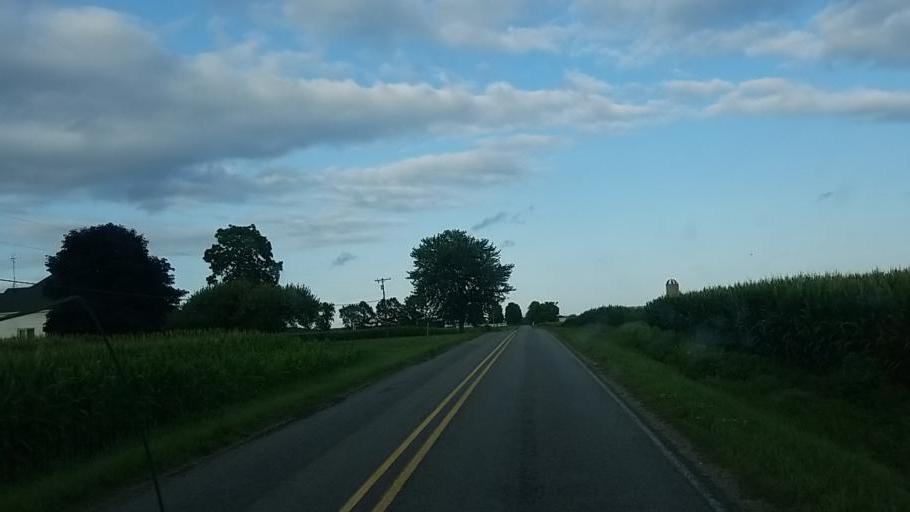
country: US
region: Michigan
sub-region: Montcalm County
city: Howard City
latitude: 43.3373
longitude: -85.3517
